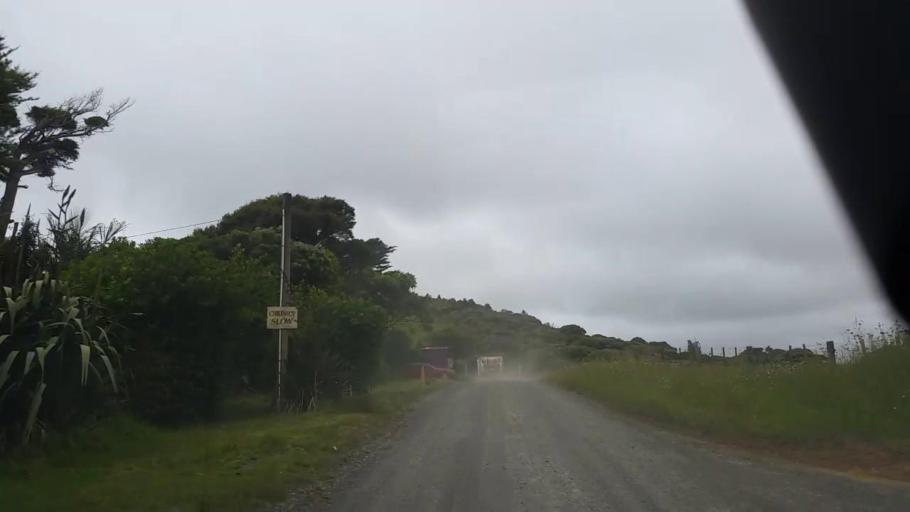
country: NZ
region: Auckland
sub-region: Auckland
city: Muriwai Beach
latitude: -36.9290
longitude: 174.4761
